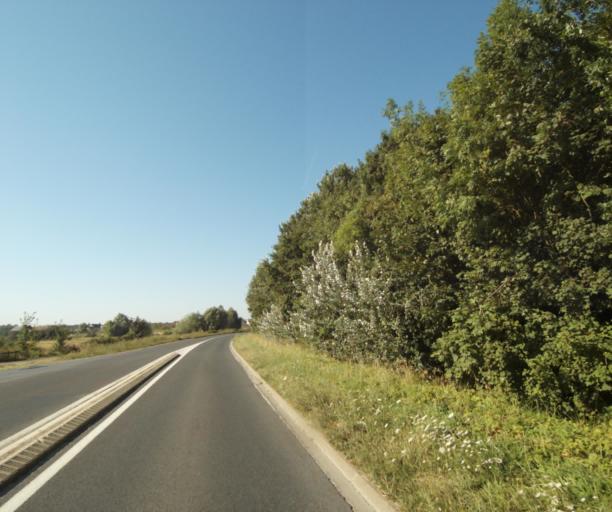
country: FR
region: Ile-de-France
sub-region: Departement de Seine-et-Marne
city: Moissy-Cramayel
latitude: 48.6369
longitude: 2.5769
